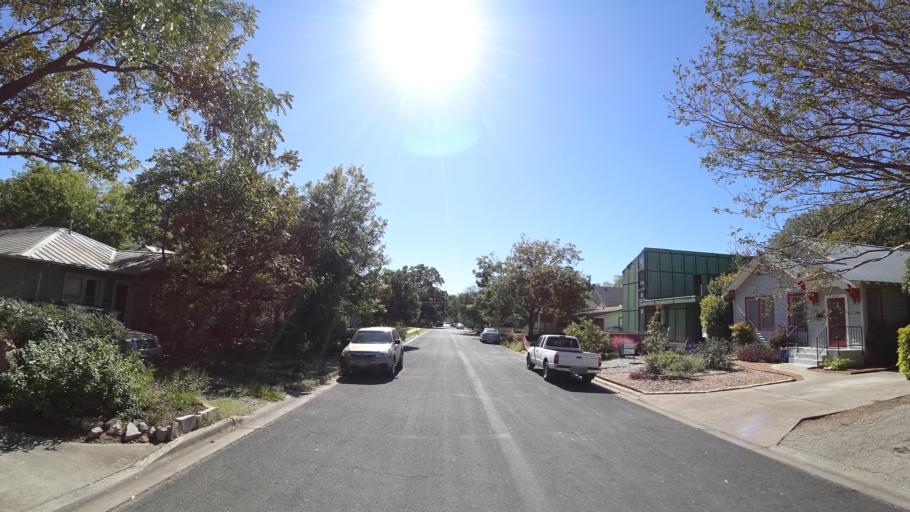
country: US
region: Texas
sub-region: Travis County
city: Austin
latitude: 30.3137
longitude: -97.7401
